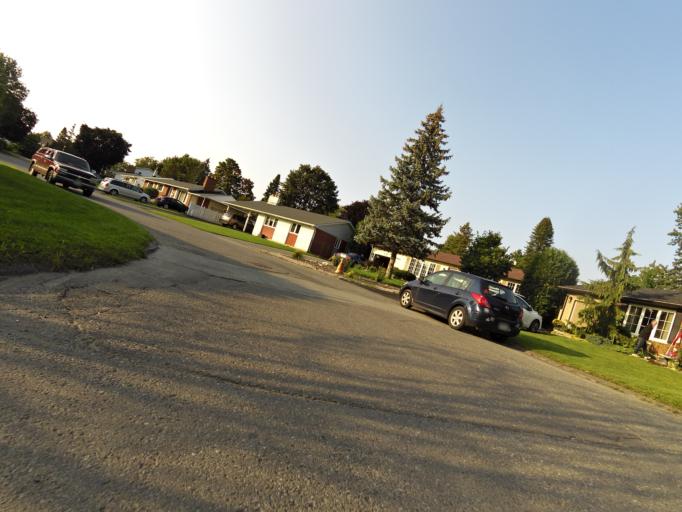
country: CA
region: Ontario
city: Bells Corners
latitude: 45.2967
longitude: -75.8814
